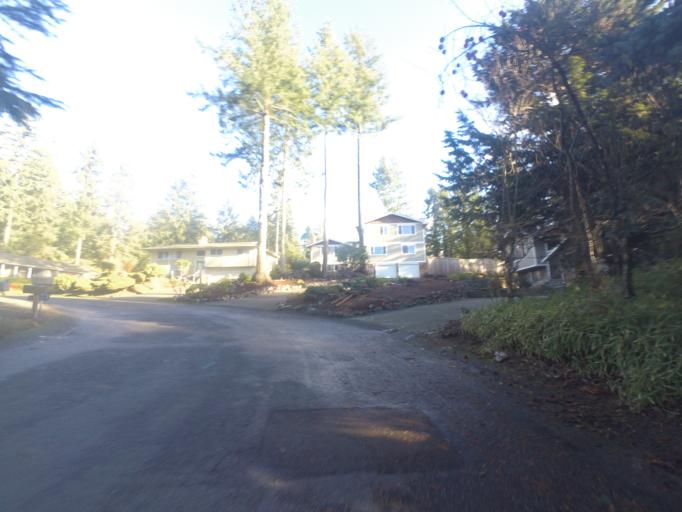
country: US
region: Washington
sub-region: Pierce County
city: University Place
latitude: 47.2107
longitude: -122.5630
